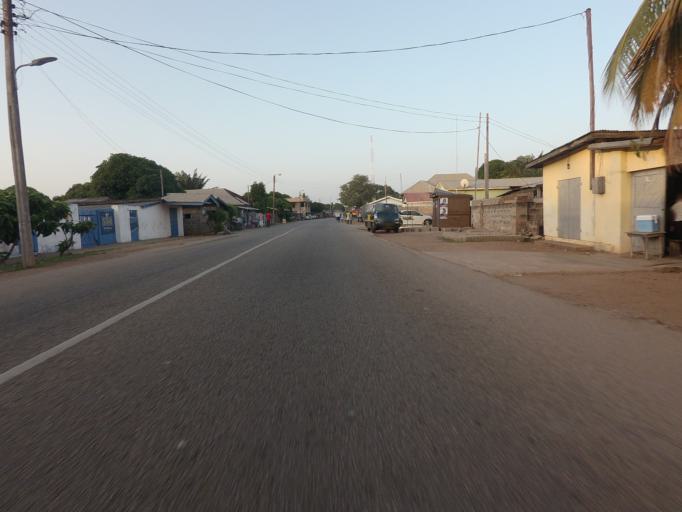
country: GH
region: Volta
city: Anloga
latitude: 5.7955
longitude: 0.9036
